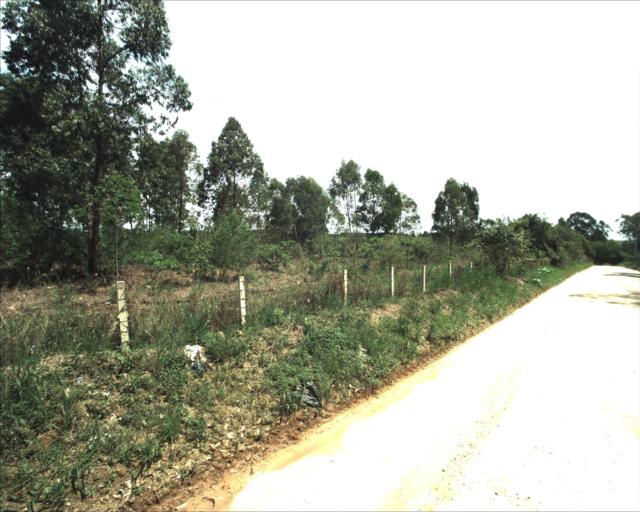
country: BR
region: Sao Paulo
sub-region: Aracoiaba Da Serra
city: Aracoiaba da Serra
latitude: -23.5553
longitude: -47.5431
